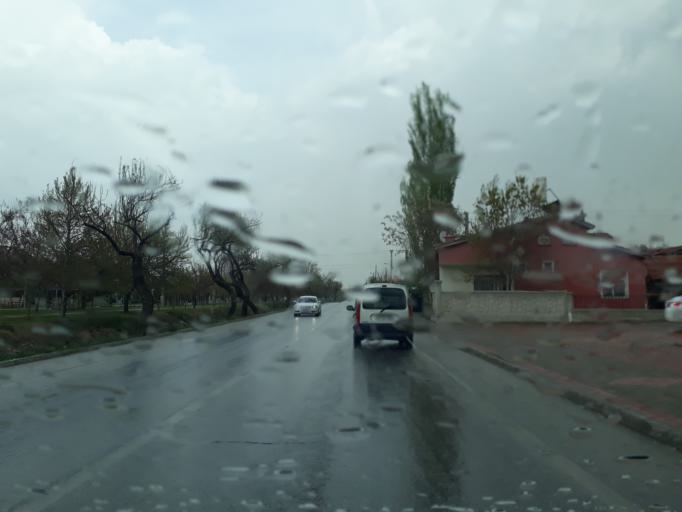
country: TR
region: Konya
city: Selcuklu
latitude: 37.9172
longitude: 32.4801
